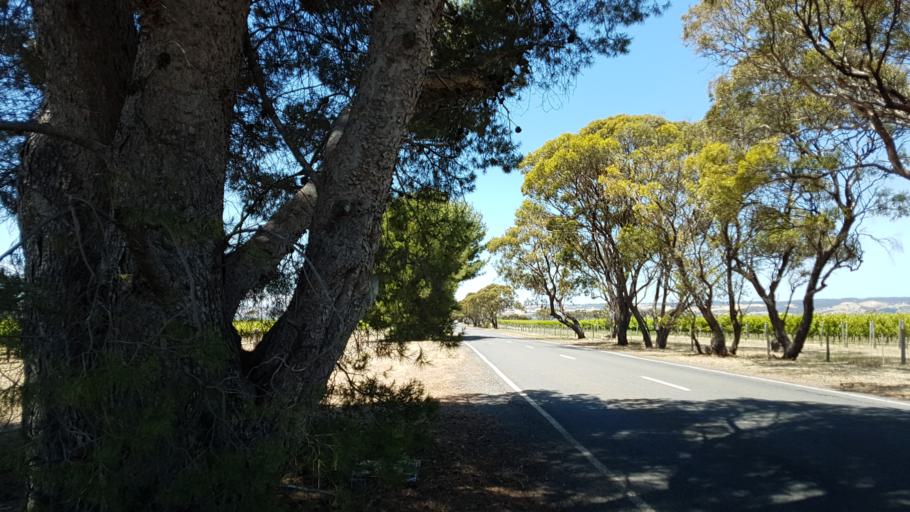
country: AU
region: South Australia
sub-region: Onkaparinga
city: McLaren Vale
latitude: -35.2315
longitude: 138.5138
